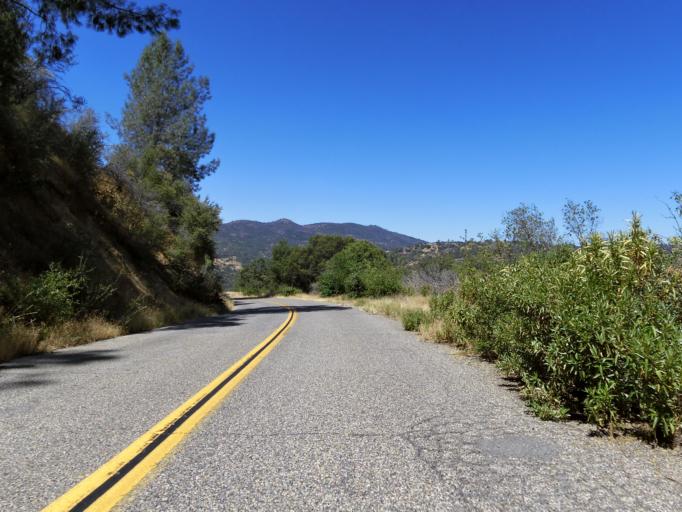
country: US
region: California
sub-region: Fresno County
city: Auberry
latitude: 37.1792
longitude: -119.5133
